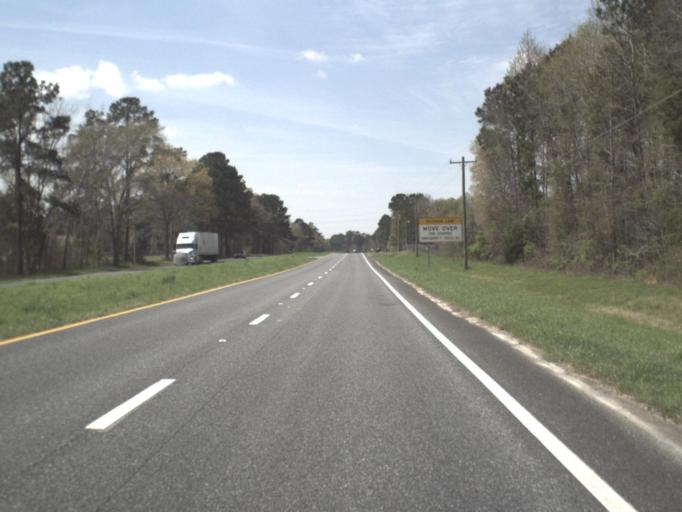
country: US
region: Florida
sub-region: Gadsden County
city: Havana
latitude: 30.6706
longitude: -84.3984
